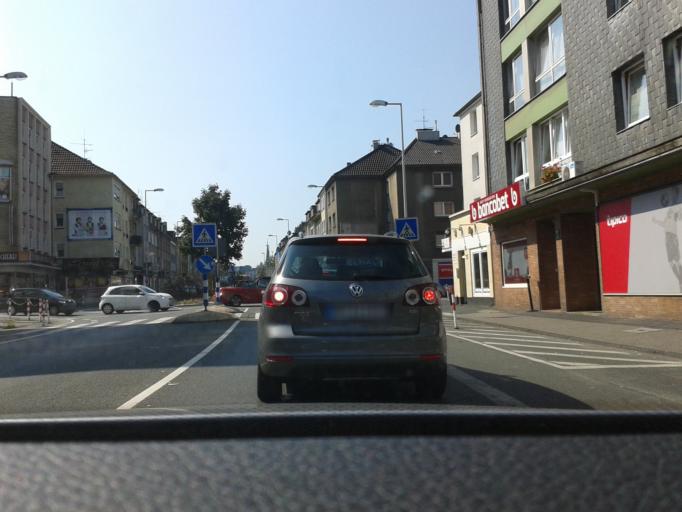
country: DE
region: North Rhine-Westphalia
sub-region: Regierungsbezirk Dusseldorf
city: Muelheim (Ruhr)
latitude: 51.4341
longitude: 6.8870
